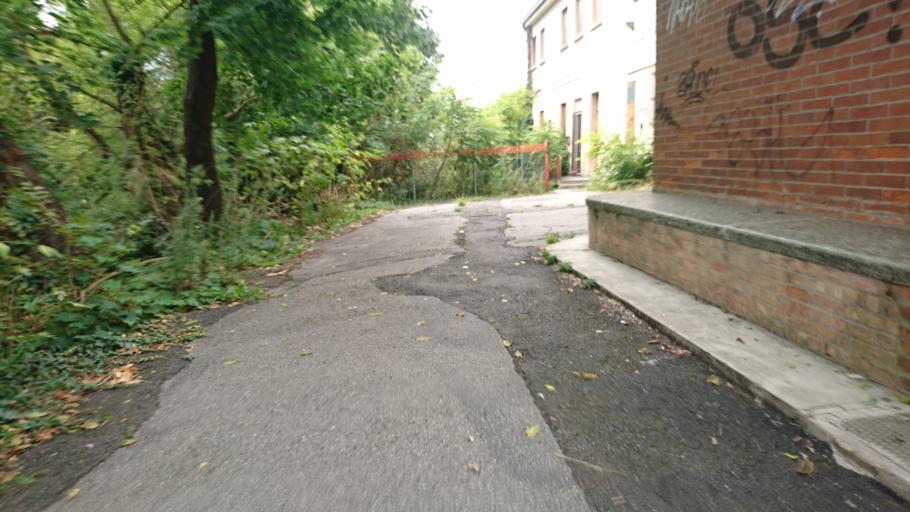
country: IT
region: Veneto
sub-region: Provincia di Padova
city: Noventa
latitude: 45.4290
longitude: 11.9479
